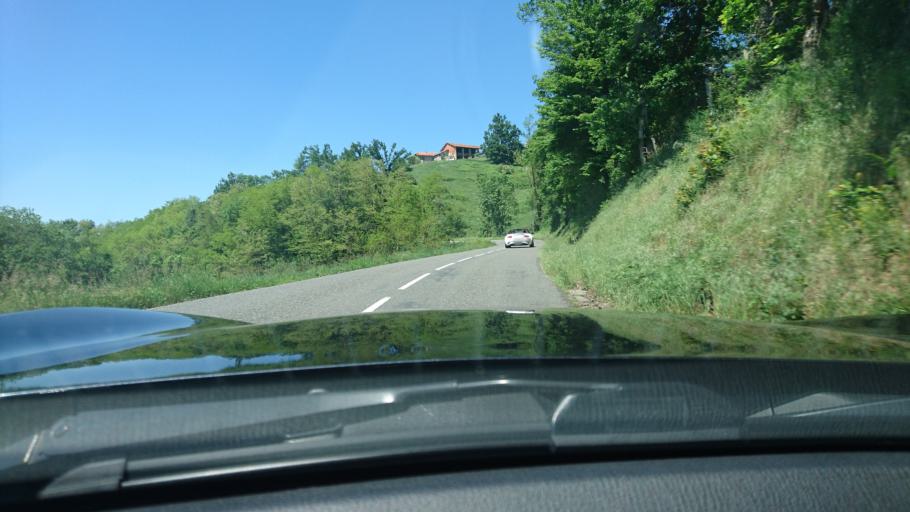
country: FR
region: Rhone-Alpes
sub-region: Departement de la Loire
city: Panissieres
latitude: 45.7824
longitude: 4.3129
